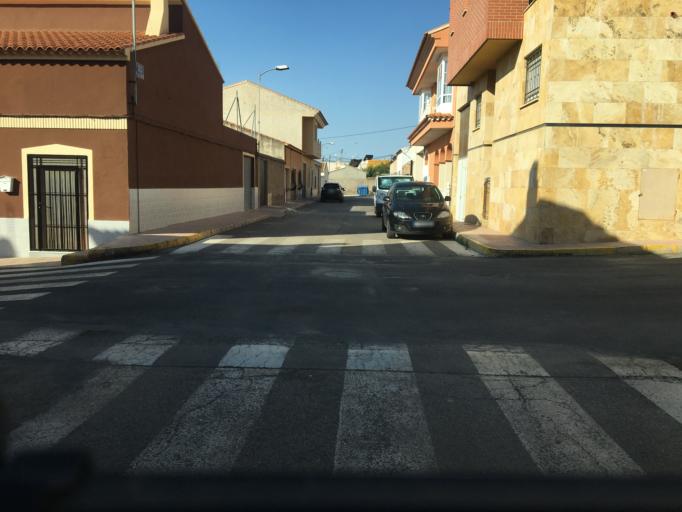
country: ES
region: Murcia
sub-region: Murcia
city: Puerto Lumbreras
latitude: 37.5532
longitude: -1.8161
